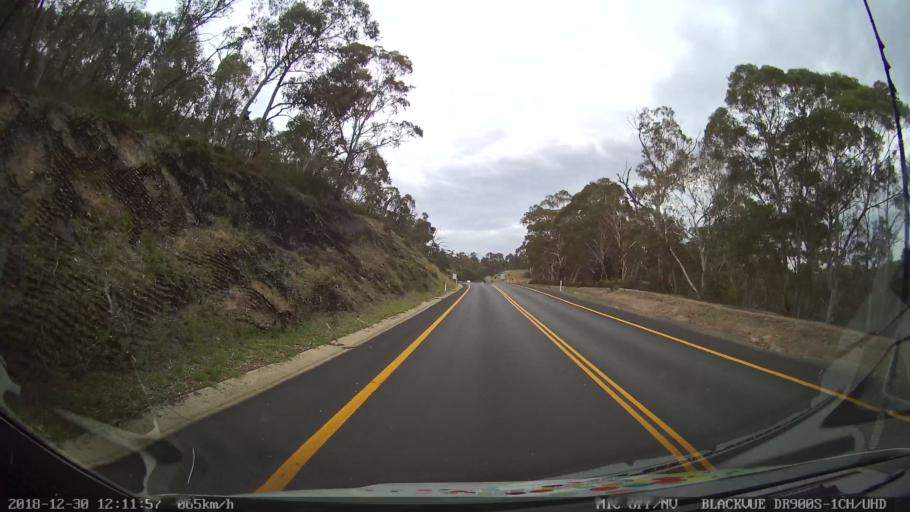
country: AU
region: New South Wales
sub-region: Snowy River
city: Jindabyne
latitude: -36.3617
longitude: 148.5872
